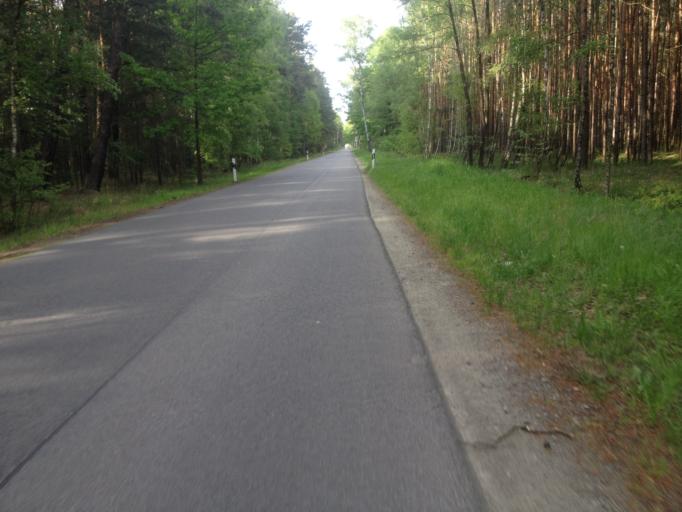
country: DE
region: Brandenburg
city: Cottbus
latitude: 51.8082
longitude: 14.3144
